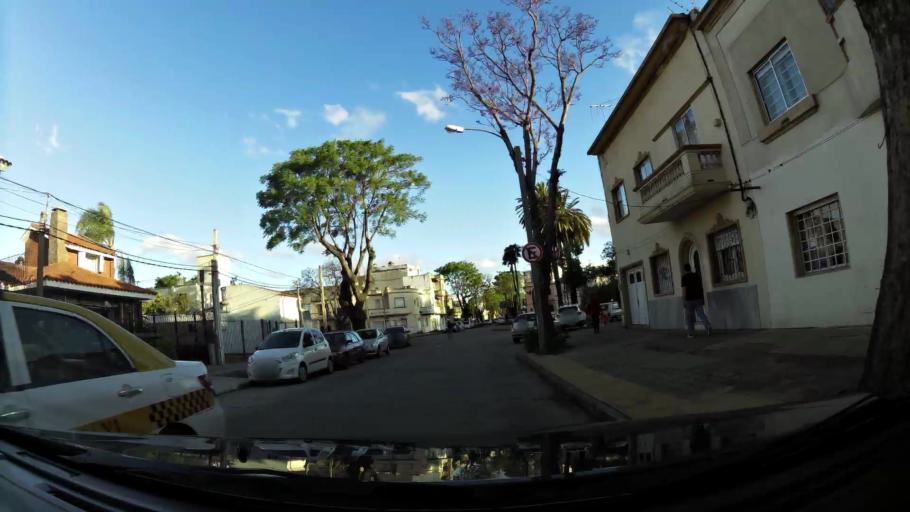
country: UY
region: Montevideo
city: Montevideo
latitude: -34.8817
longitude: -56.1489
